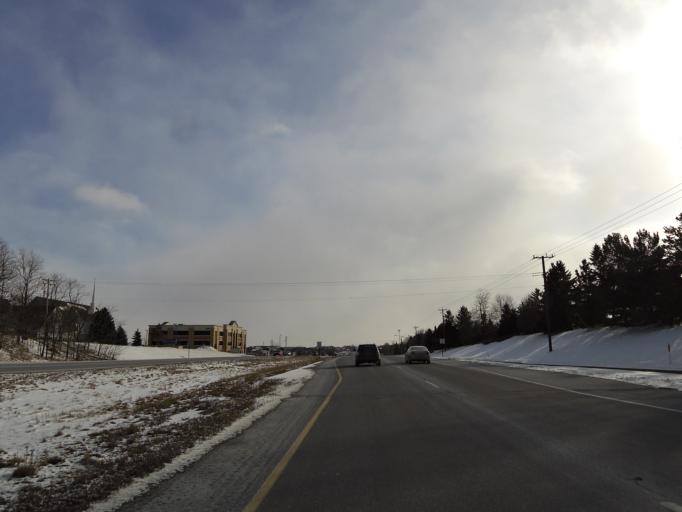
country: US
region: Minnesota
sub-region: Washington County
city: Woodbury
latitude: 44.9269
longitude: -92.9342
